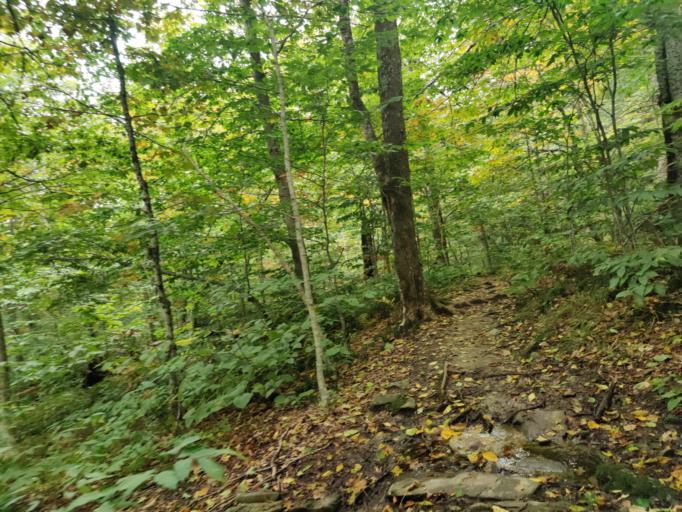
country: US
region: Vermont
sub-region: Bennington County
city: Manchester Center
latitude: 43.2653
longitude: -72.9411
